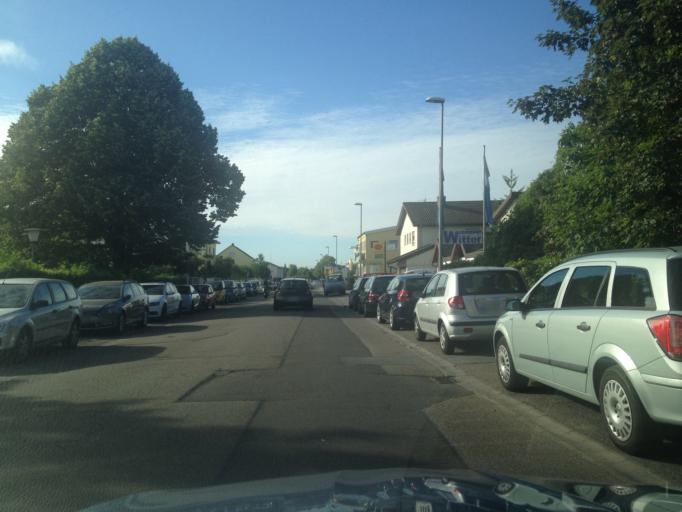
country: DE
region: Baden-Wuerttemberg
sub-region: Karlsruhe Region
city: Schwetzingen
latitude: 49.3784
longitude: 8.5856
